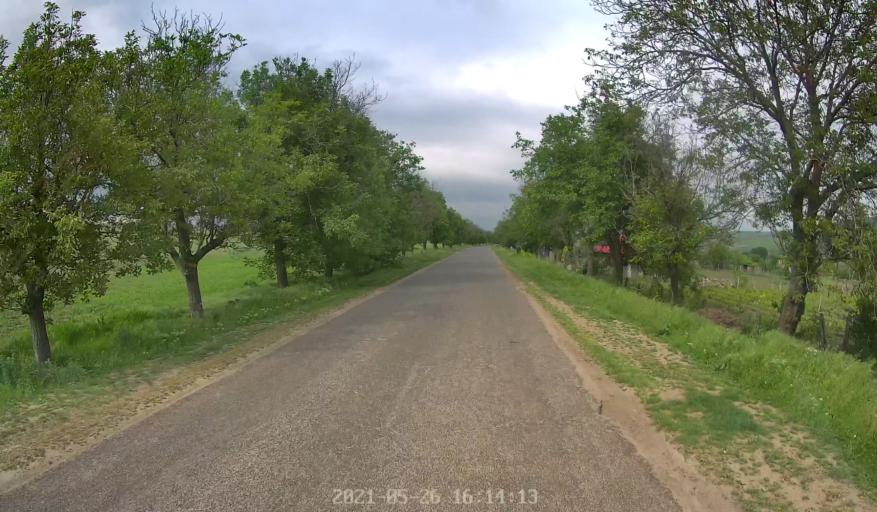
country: MD
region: Hincesti
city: Dancu
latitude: 46.7080
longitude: 28.3406
